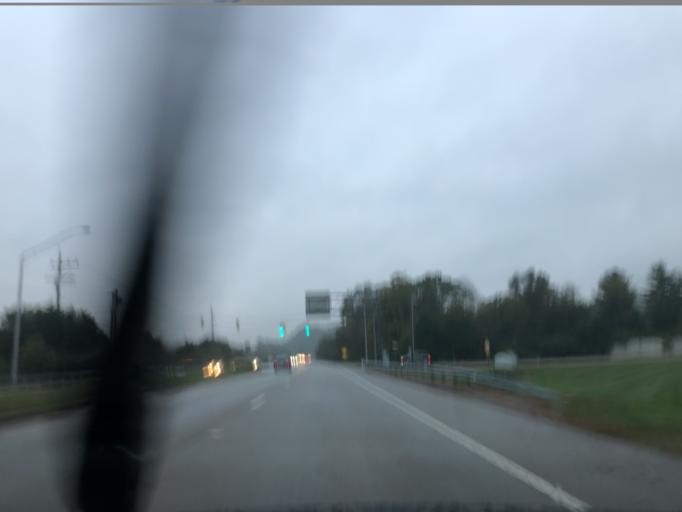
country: US
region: Ohio
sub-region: Hamilton County
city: The Village of Indian Hill
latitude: 39.2399
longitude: -84.3006
